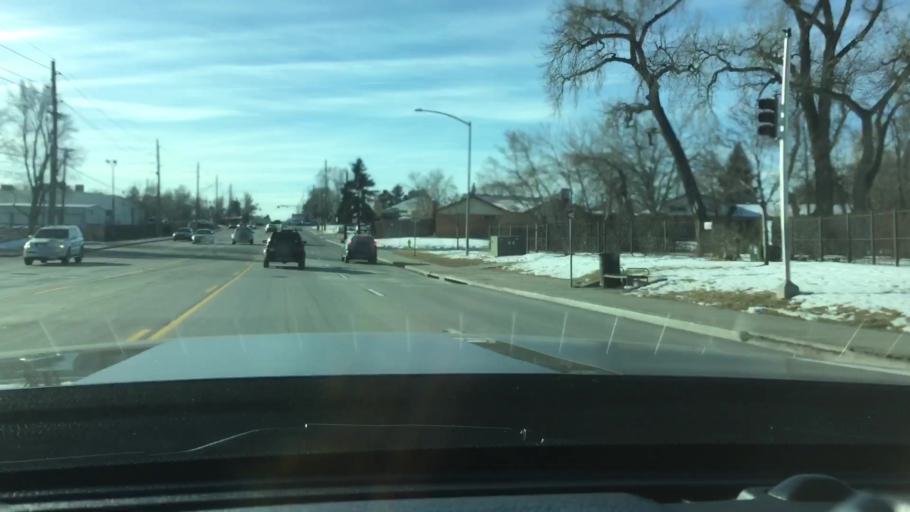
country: US
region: Colorado
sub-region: Adams County
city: Northglenn
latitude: 39.8879
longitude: -104.9967
